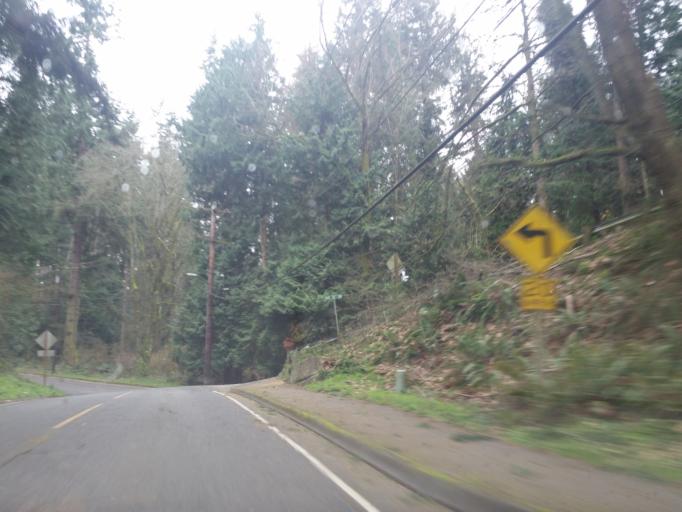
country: US
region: Washington
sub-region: Snohomish County
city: Meadowdale
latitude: 47.8502
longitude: -122.3277
